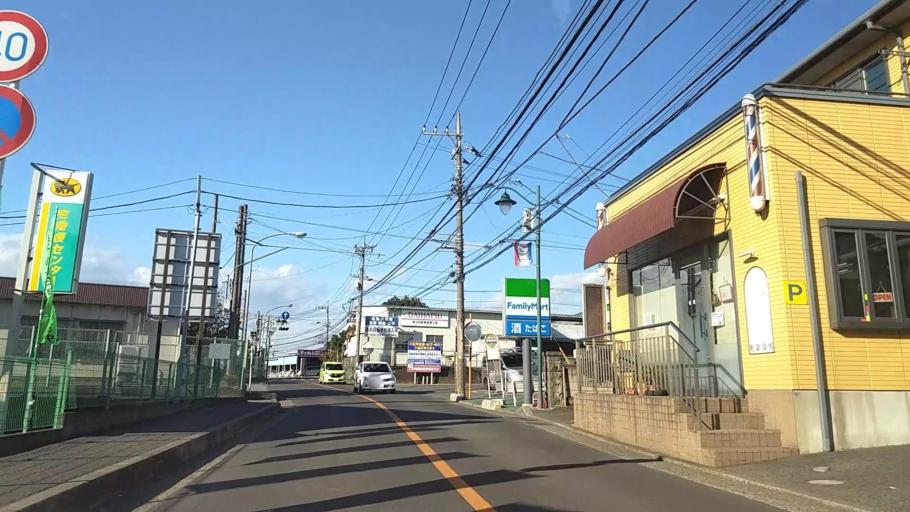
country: JP
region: Tokyo
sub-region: Machida-shi
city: Machida
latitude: 35.5340
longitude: 139.5461
